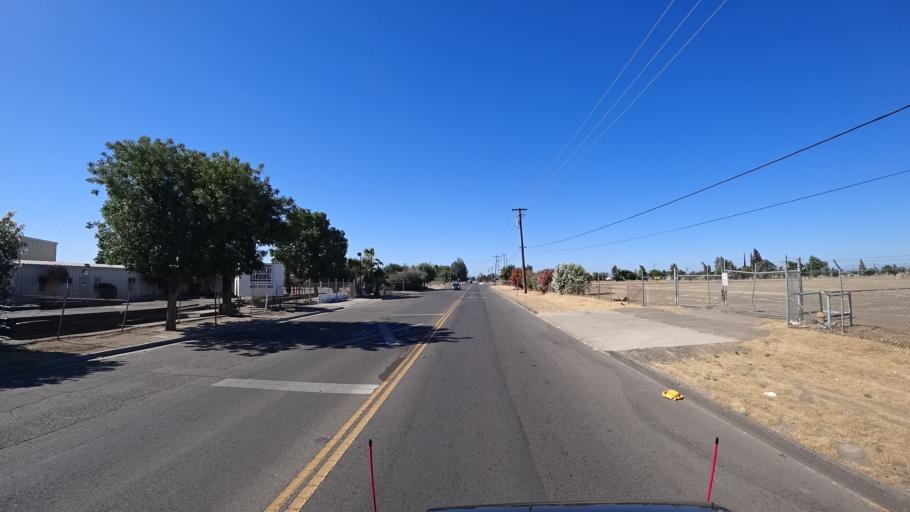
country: US
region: California
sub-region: Fresno County
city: West Park
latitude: 36.7448
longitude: -119.8356
